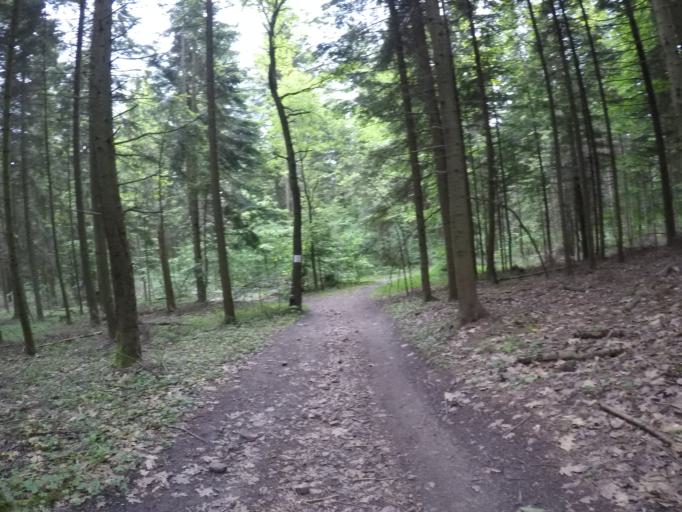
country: PL
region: Swietokrzyskie
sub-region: Powiat kielecki
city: Kielce
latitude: 50.8365
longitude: 20.6008
